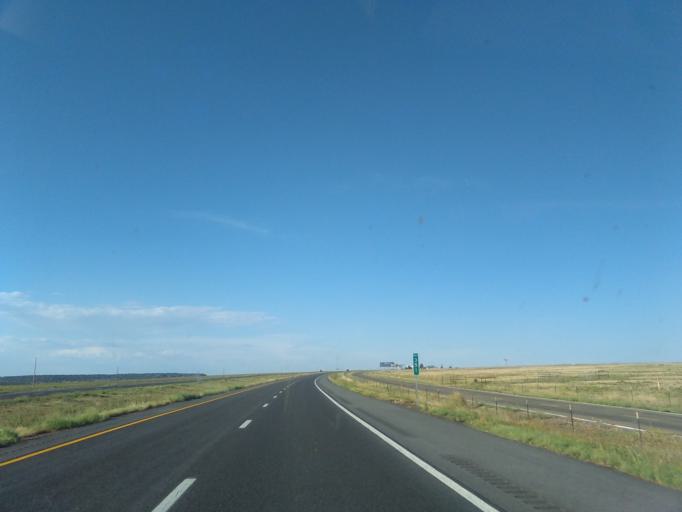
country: US
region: New Mexico
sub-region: San Miguel County
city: Las Vegas
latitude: 35.6645
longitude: -105.1851
